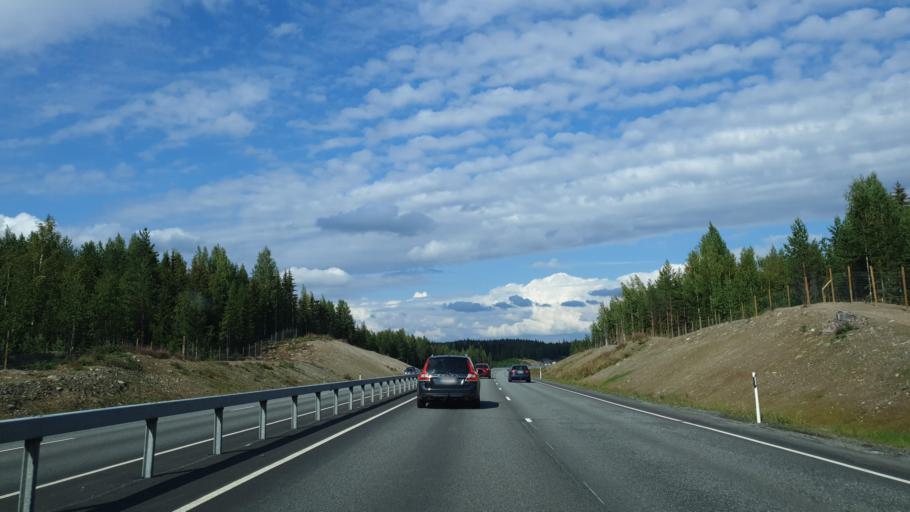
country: FI
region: Southern Savonia
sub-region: Pieksaemaeki
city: Juva
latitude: 61.8121
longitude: 27.6069
